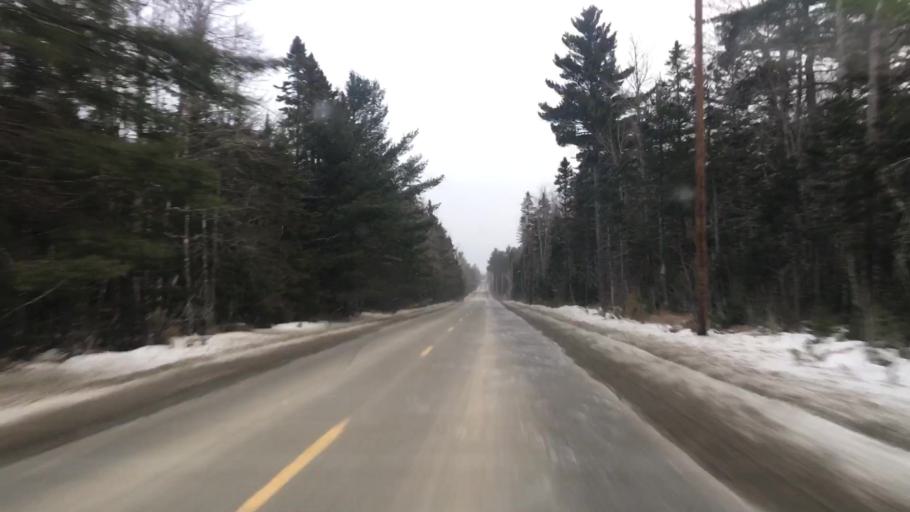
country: US
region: Maine
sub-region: Hancock County
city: Ellsworth
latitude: 44.6689
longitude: -68.3548
